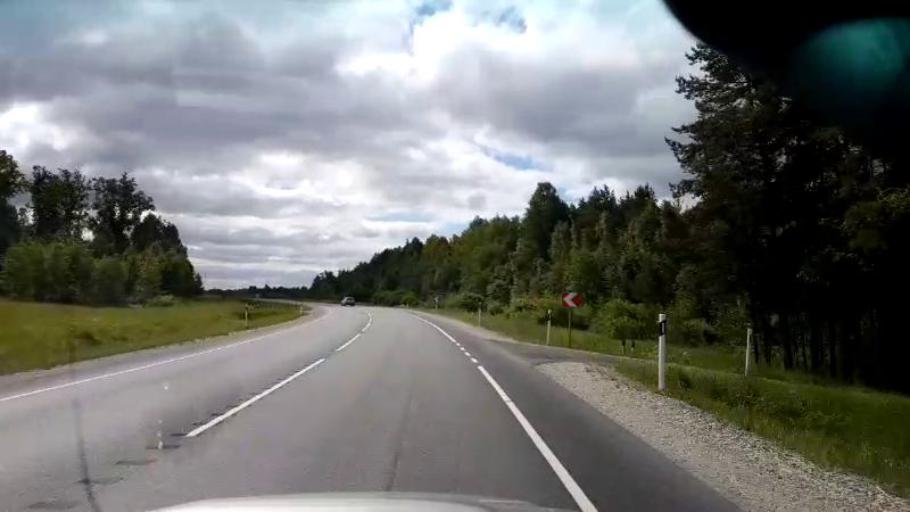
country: EE
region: Paernumaa
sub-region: Halinga vald
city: Parnu-Jaagupi
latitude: 58.6724
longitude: 24.4465
